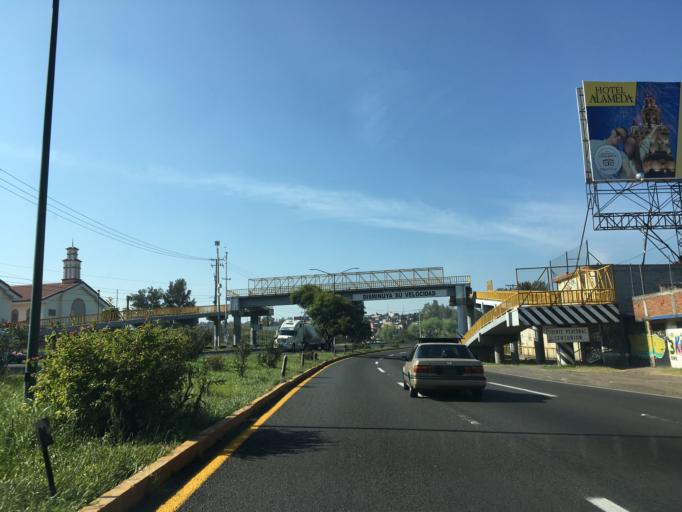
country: MX
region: Michoacan
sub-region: Tarimbaro
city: Fraccionamiento Privadas del Sol
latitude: 19.7399
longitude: -101.1774
